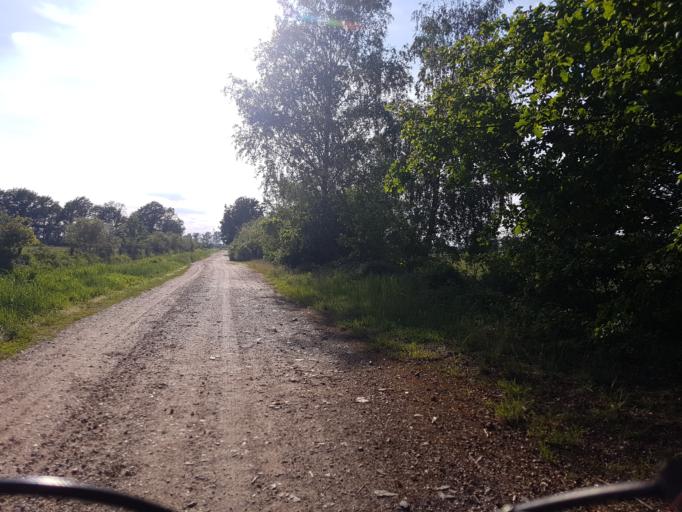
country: DE
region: Brandenburg
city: Merzdorf
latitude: 51.4206
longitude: 13.5373
